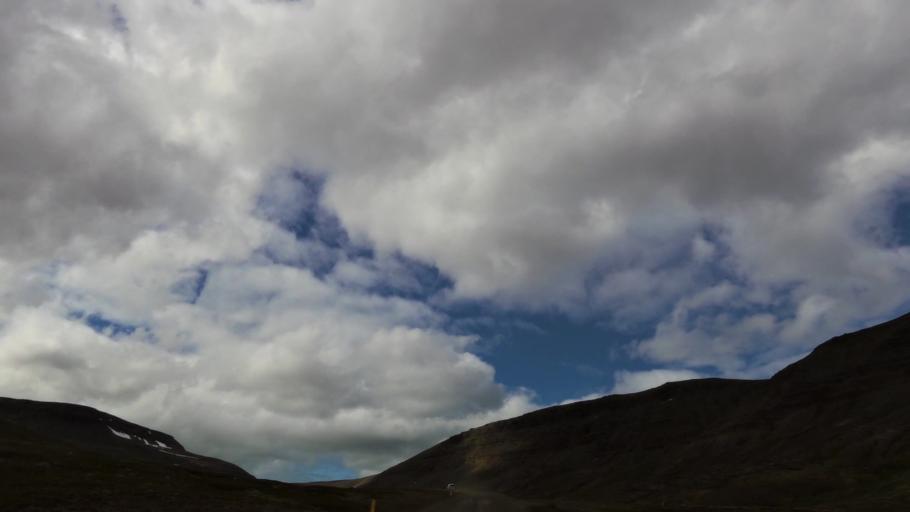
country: IS
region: Westfjords
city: Isafjoerdur
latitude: 66.1604
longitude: -23.3001
